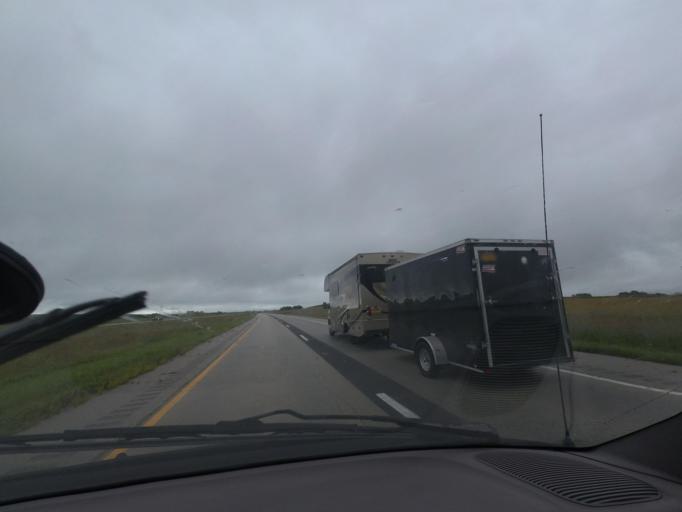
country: US
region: Illinois
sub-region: Sangamon County
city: Riverton
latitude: 39.8385
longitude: -89.3794
